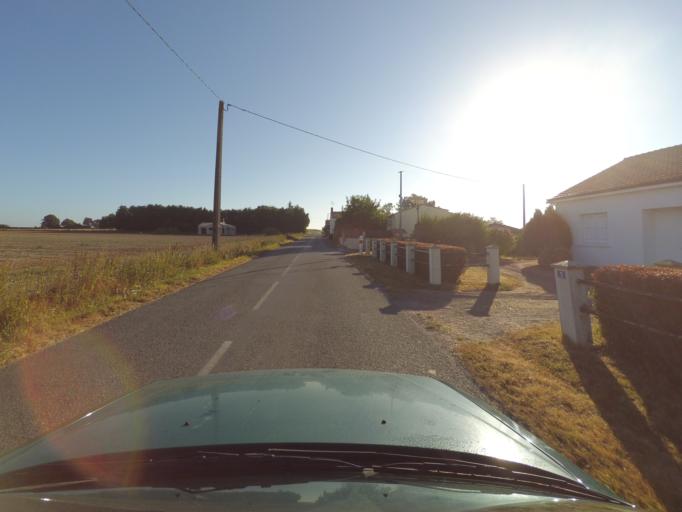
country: FR
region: Pays de la Loire
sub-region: Departement de la Loire-Atlantique
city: Montbert
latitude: 47.0654
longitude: -1.4768
